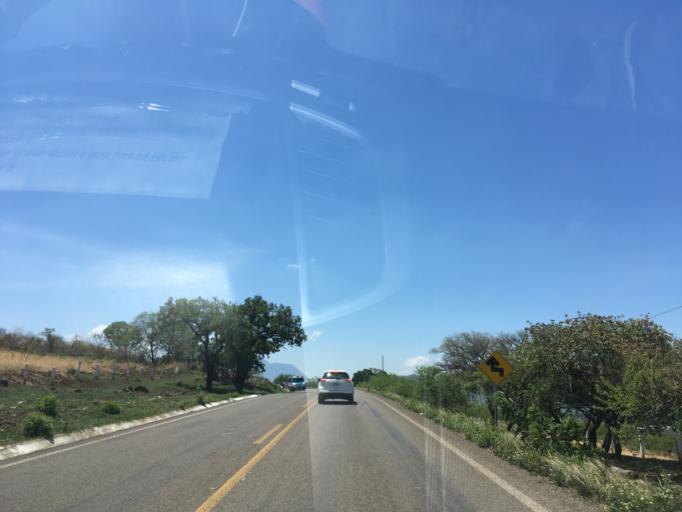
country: MX
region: Michoacan
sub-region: Tuxpan
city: La Soledad
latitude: 19.4959
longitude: -100.4584
